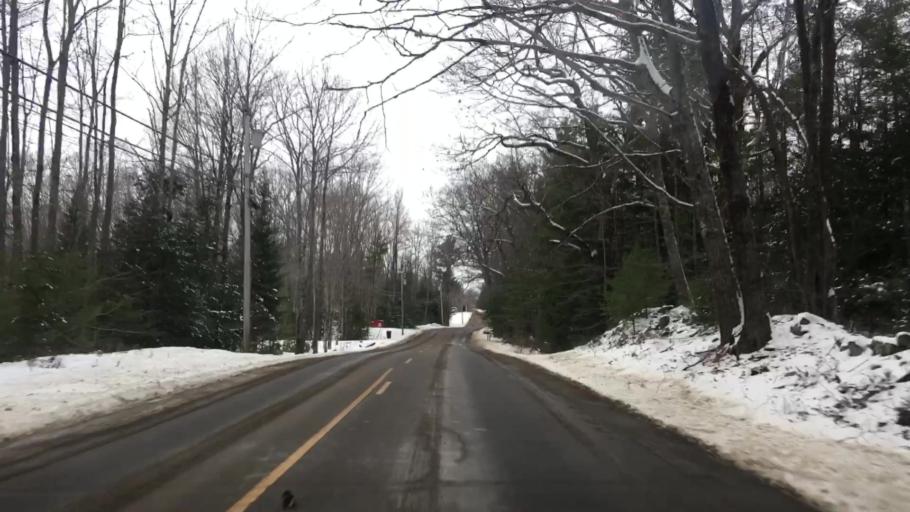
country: US
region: Maine
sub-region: Kennebec County
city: Chelsea
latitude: 44.2516
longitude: -69.6378
